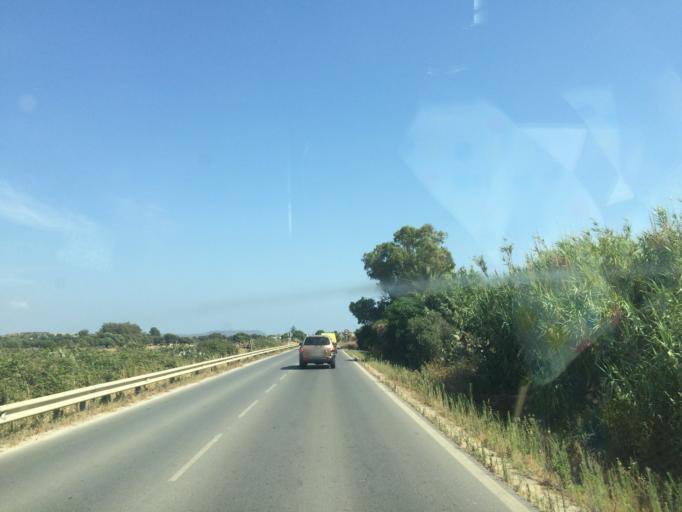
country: ES
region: Andalusia
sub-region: Provincia de Cadiz
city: Conil de la Frontera
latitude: 36.2499
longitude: -6.0676
